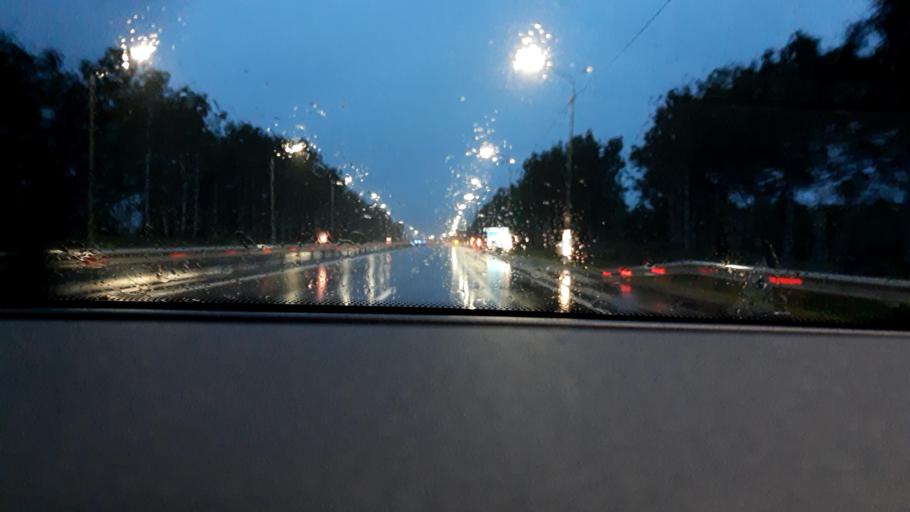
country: RU
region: Nizjnij Novgorod
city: Burevestnik
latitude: 56.0601
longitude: 43.9444
